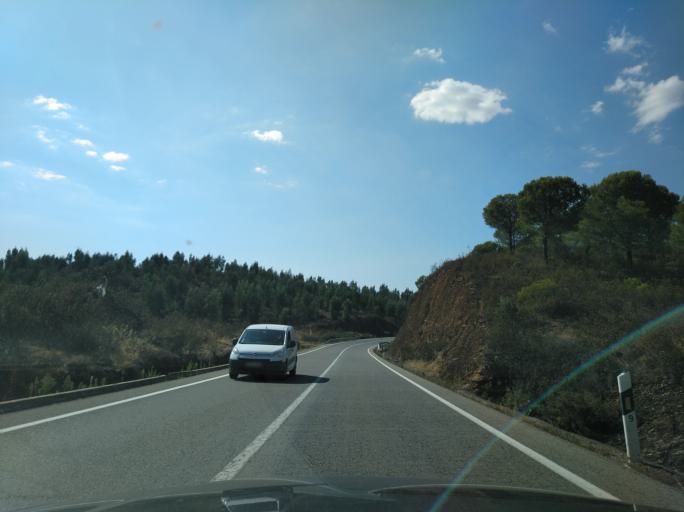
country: ES
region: Andalusia
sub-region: Provincia de Huelva
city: Santa Barbara de Casa
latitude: 37.8037
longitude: -7.2004
